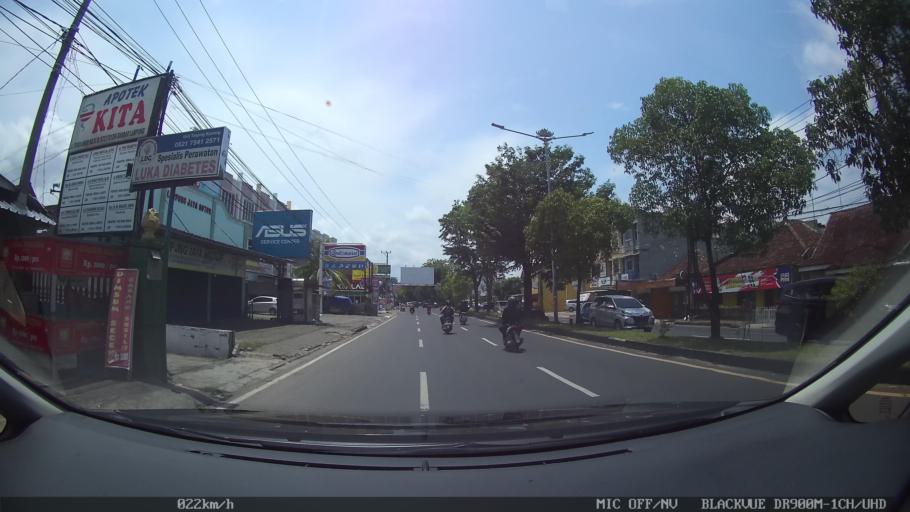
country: ID
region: Lampung
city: Kedaton
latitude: -5.4011
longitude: 105.2608
